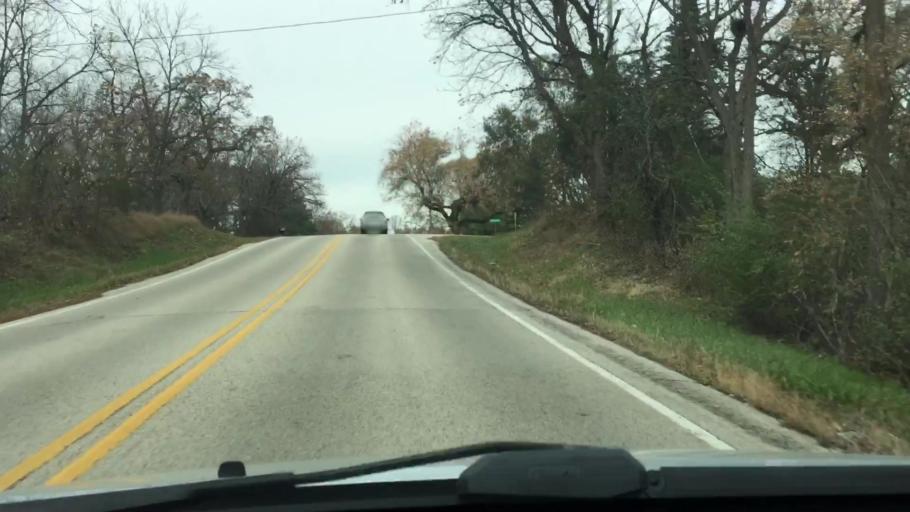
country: US
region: Wisconsin
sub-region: Waukesha County
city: North Prairie
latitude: 42.9060
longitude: -88.4062
